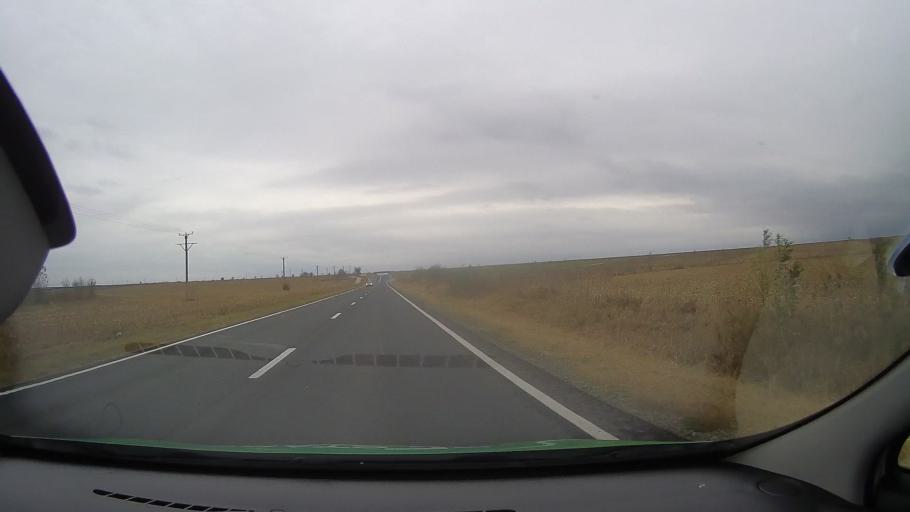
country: RO
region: Constanta
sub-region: Comuna Nicolae Balcescu
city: Nicolae Balcescu
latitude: 44.3840
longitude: 28.3968
